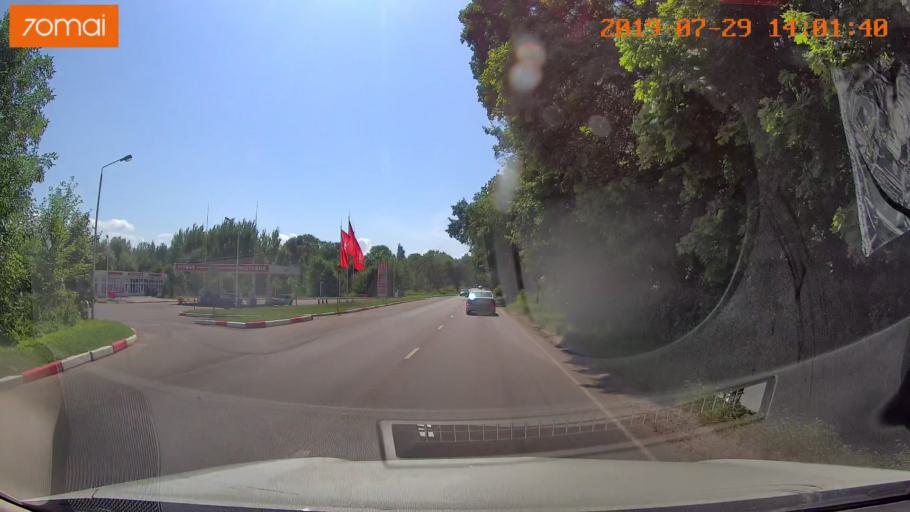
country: RU
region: Kaliningrad
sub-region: Gorod Kaliningrad
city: Baltiysk
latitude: 54.6687
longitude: 19.9201
